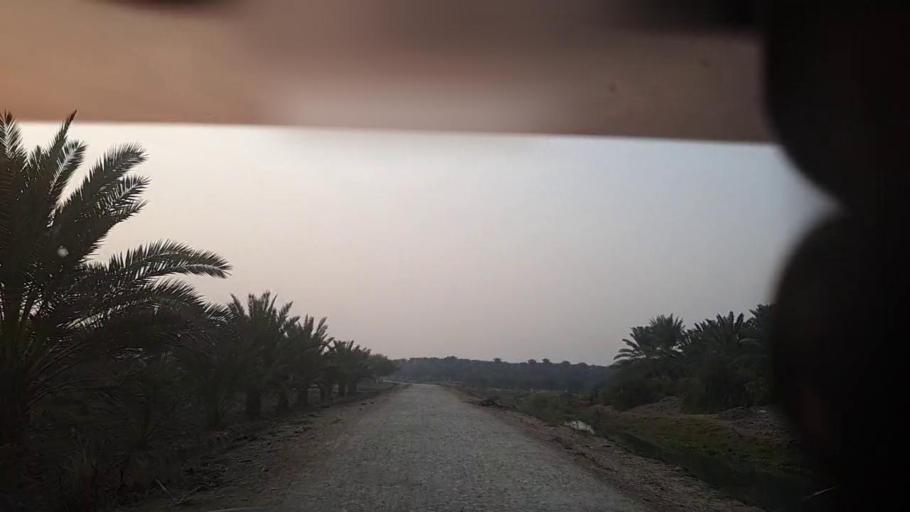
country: PK
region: Sindh
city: Pir jo Goth
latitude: 27.5217
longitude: 68.6450
